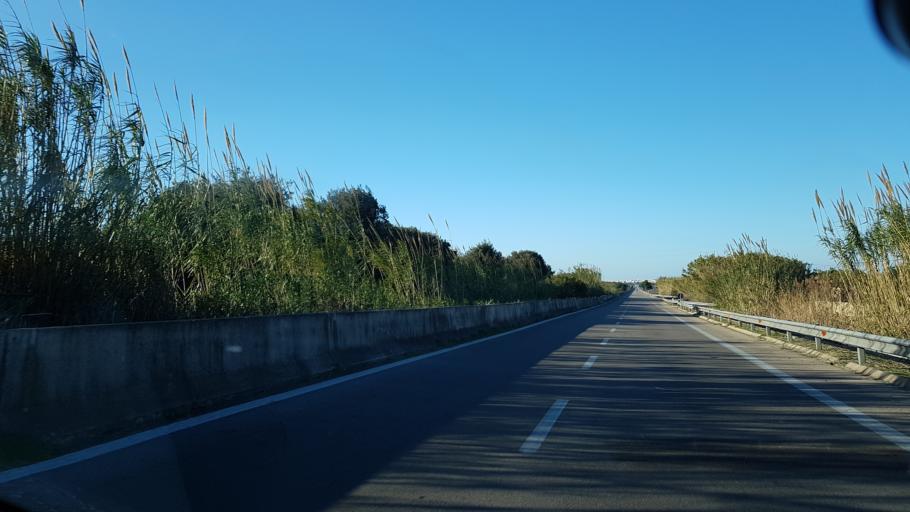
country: IT
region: Apulia
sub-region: Provincia di Lecce
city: Alezio
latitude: 40.0158
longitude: 18.0474
